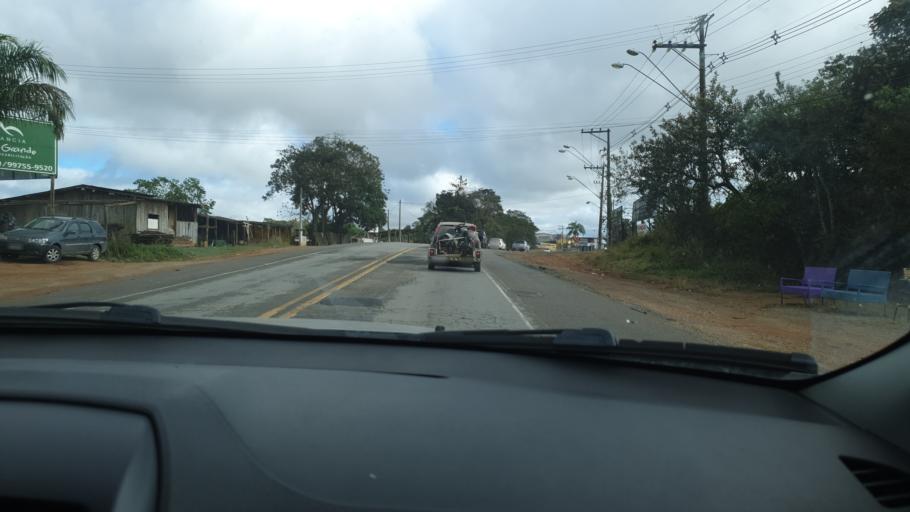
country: BR
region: Sao Paulo
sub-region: Ibiuna
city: Ibiuna
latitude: -23.6604
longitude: -47.1960
